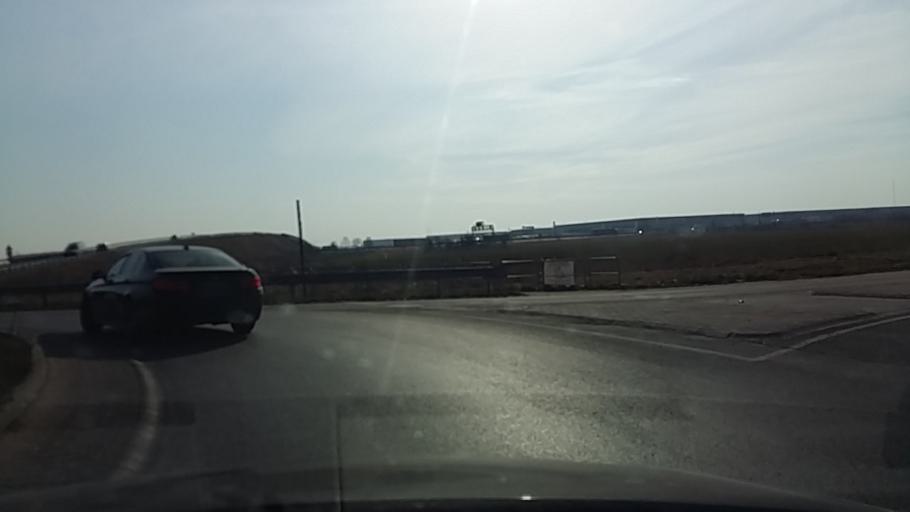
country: HU
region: Pest
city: Szigetszentmiklos
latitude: 47.3823
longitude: 19.0330
